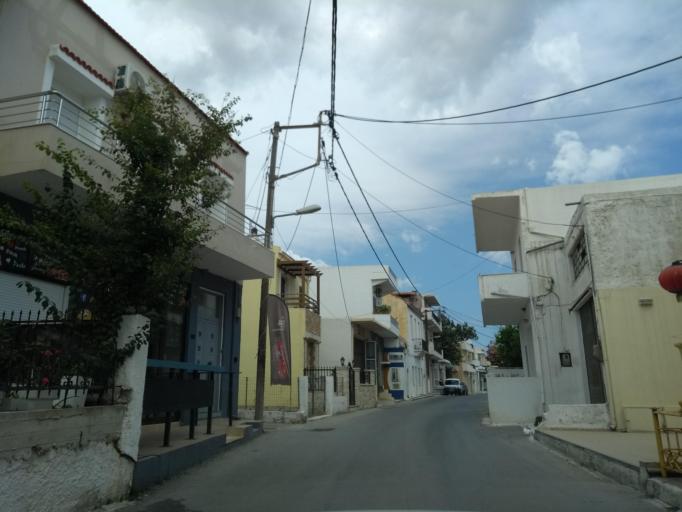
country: GR
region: Crete
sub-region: Nomos Chanias
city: Kalivai
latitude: 35.4537
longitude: 24.1719
